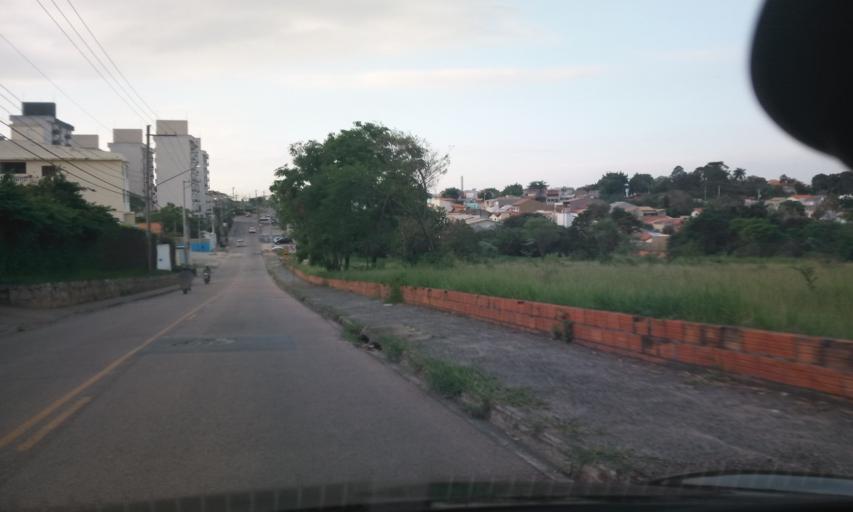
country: BR
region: Sao Paulo
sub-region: Itupeva
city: Itupeva
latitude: -23.1840
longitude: -46.9854
